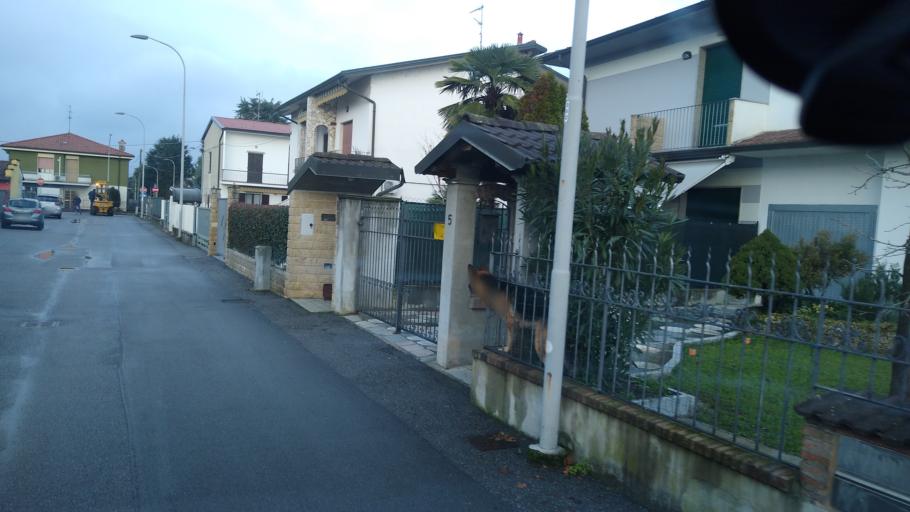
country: IT
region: Lombardy
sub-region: Provincia di Bergamo
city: Misano di Gera d'Adda
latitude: 45.4680
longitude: 9.6240
